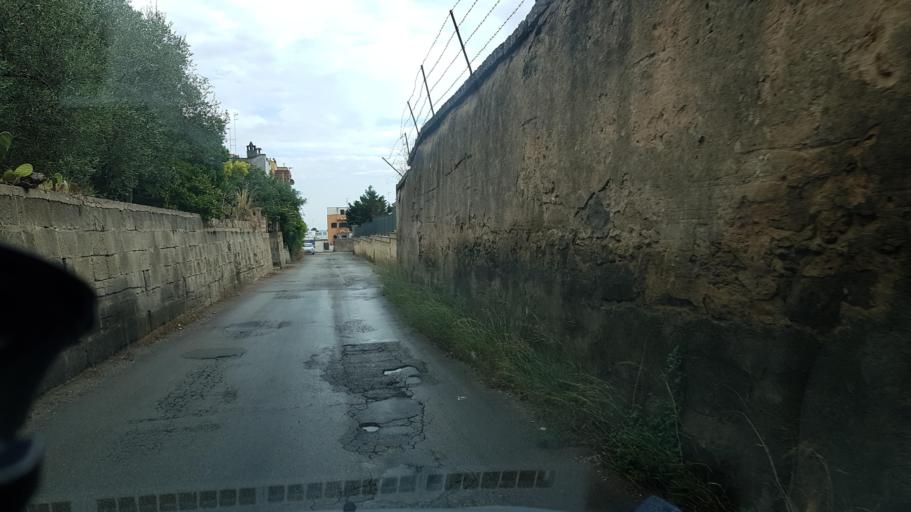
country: IT
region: Apulia
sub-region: Provincia di Brindisi
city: Oria
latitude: 40.4975
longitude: 17.6521
